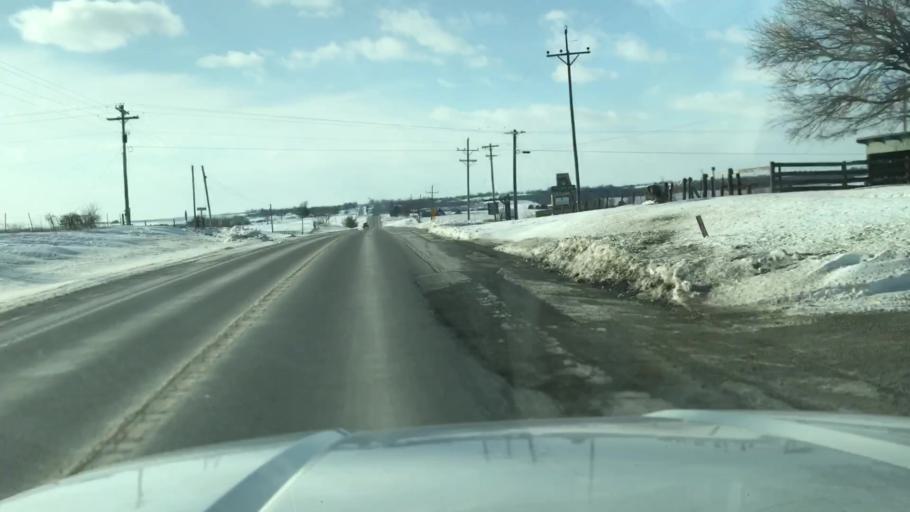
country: US
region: Missouri
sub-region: Nodaway County
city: Maryville
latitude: 40.3443
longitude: -94.7595
